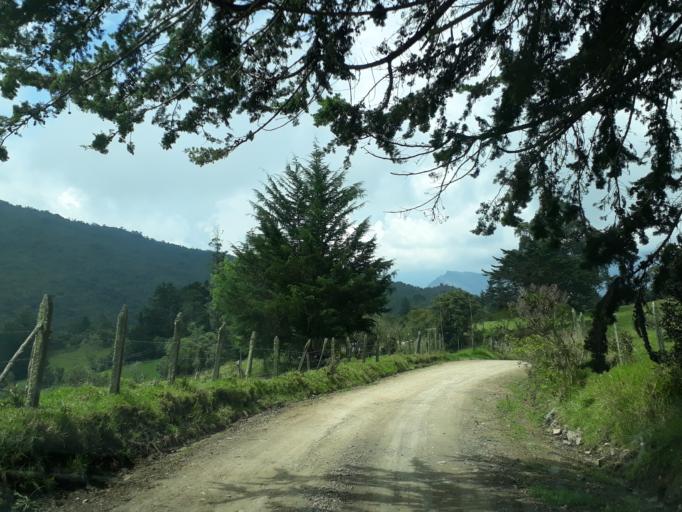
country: CO
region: Cundinamarca
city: Macheta
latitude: 5.1075
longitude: -73.5402
